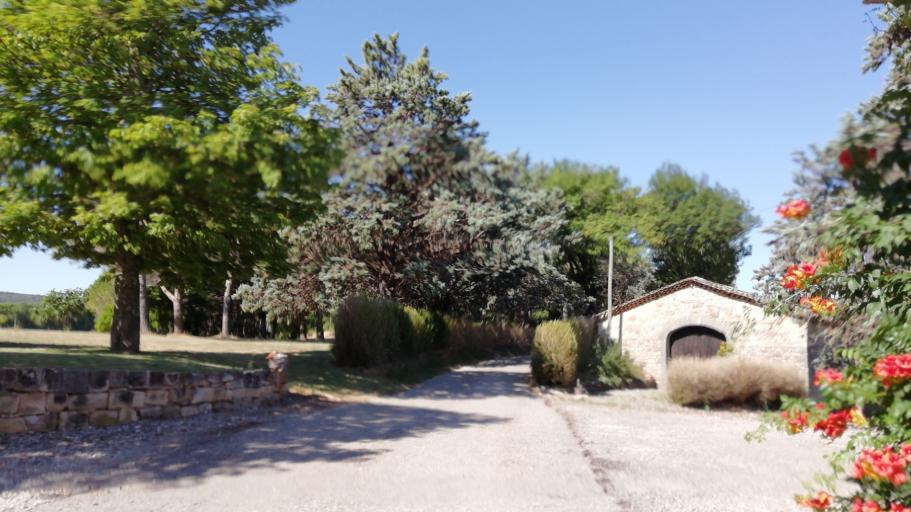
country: FR
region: Languedoc-Roussillon
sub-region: Departement de l'Herault
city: Saint-Martin-de-Londres
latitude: 43.7910
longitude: 3.7486
